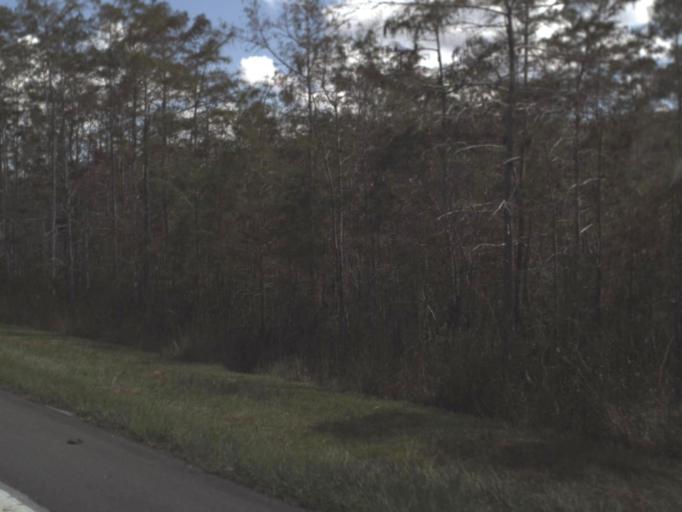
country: US
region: Florida
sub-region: Miami-Dade County
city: Kendall West
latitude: 25.8489
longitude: -80.9551
